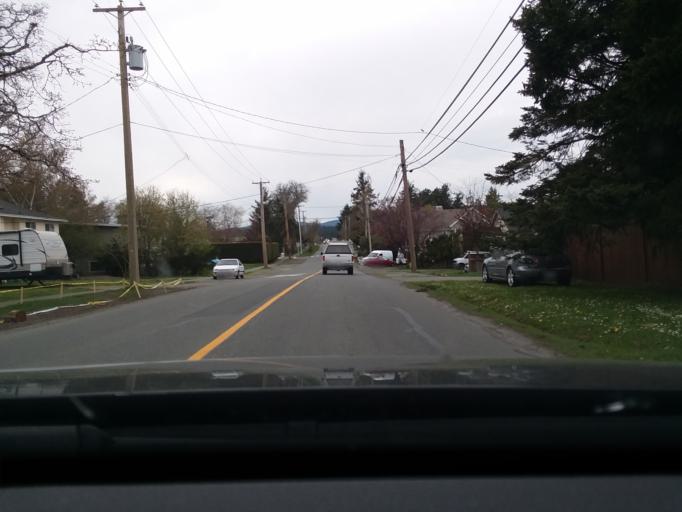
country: CA
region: British Columbia
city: Victoria
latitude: 48.4792
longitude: -123.4153
